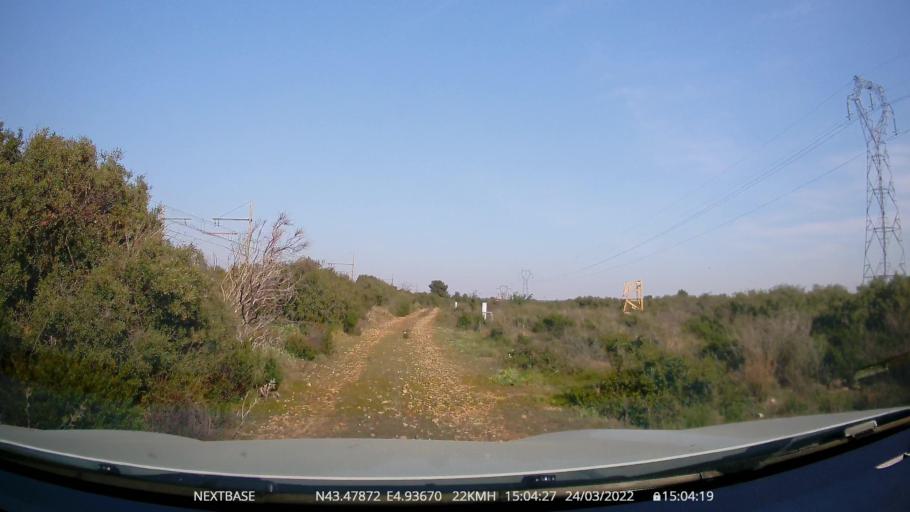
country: FR
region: Provence-Alpes-Cote d'Azur
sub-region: Departement des Bouches-du-Rhone
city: Fos-sur-Mer
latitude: 43.4787
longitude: 4.9366
